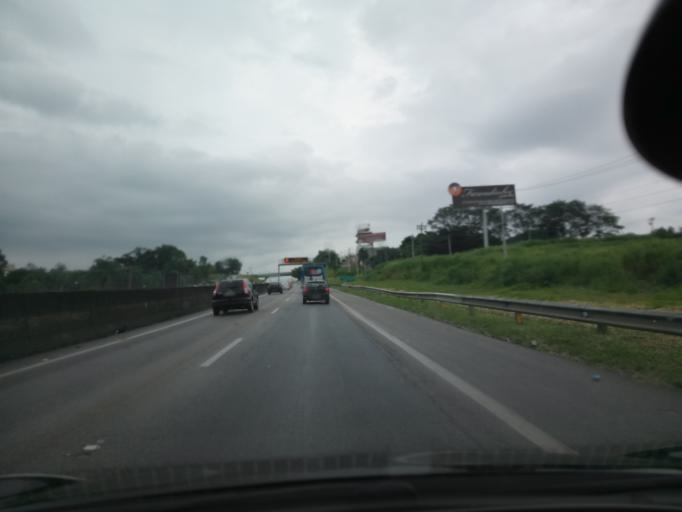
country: BR
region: Sao Paulo
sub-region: Campinas
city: Campinas
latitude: -22.9689
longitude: -47.1012
